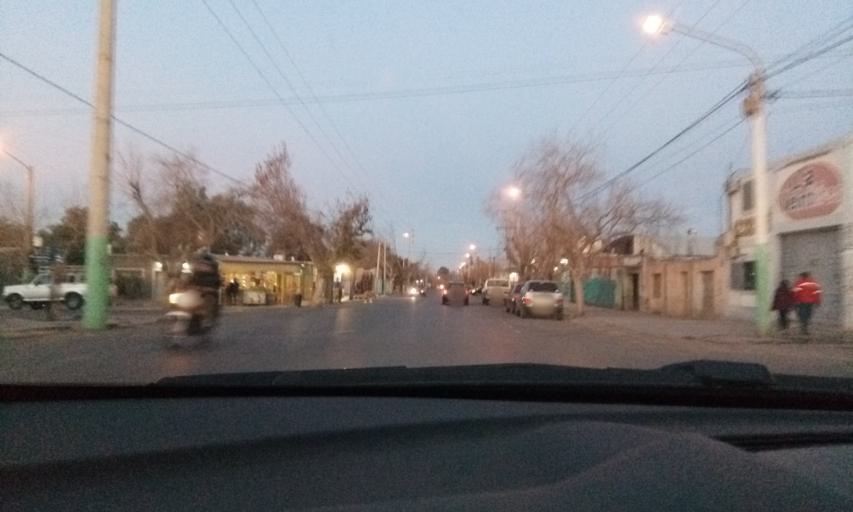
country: AR
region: San Juan
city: San Juan
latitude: -31.5530
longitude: -68.5551
